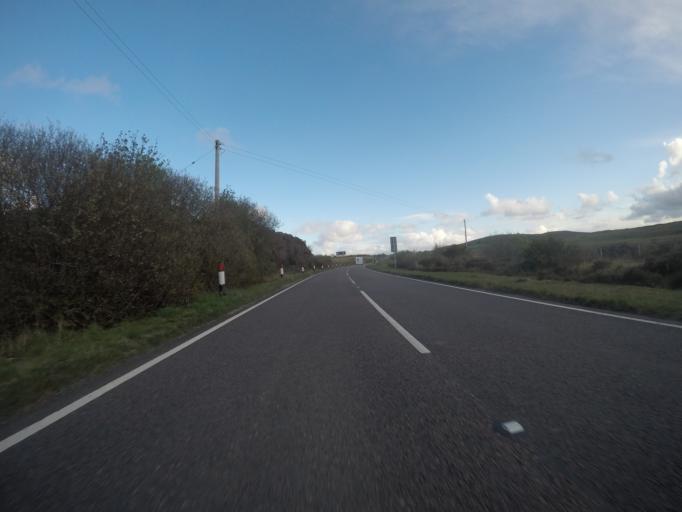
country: GB
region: Scotland
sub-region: Highland
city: Portree
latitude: 57.4800
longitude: -6.3006
